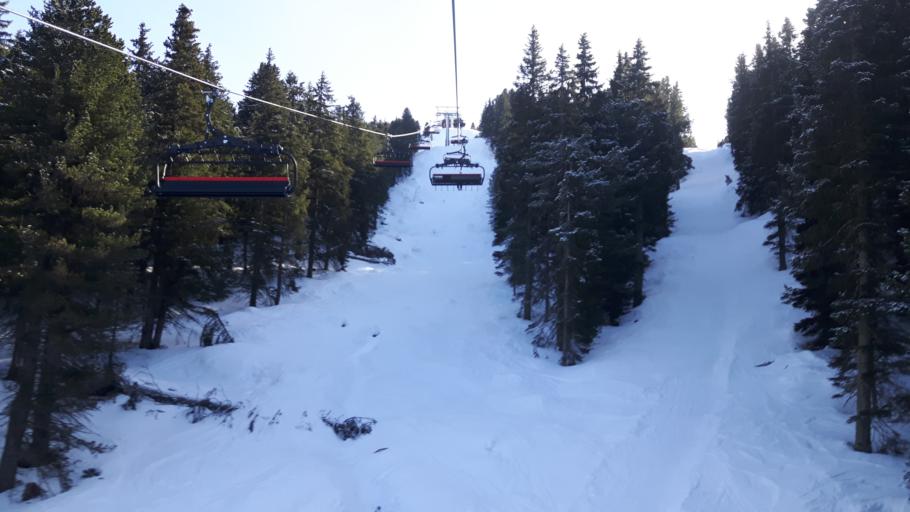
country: IT
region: Trentino-Alto Adige
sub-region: Provincia di Trento
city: Tesero
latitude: 46.3566
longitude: 11.5346
